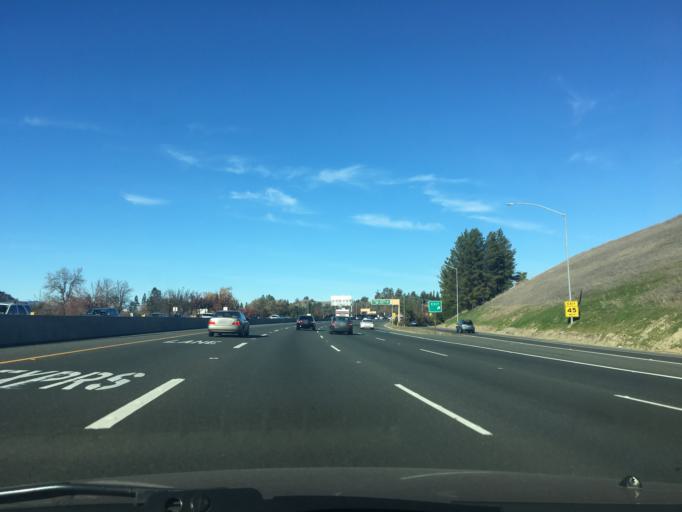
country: US
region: California
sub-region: Contra Costa County
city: Alamo
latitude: 37.8486
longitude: -122.0280
